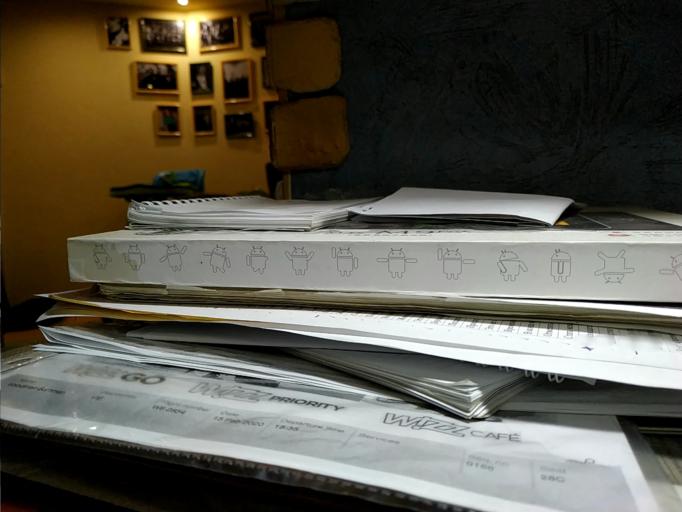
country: RU
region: Arkhangelskaya
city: Kargopol'
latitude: 61.6345
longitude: 39.2441
